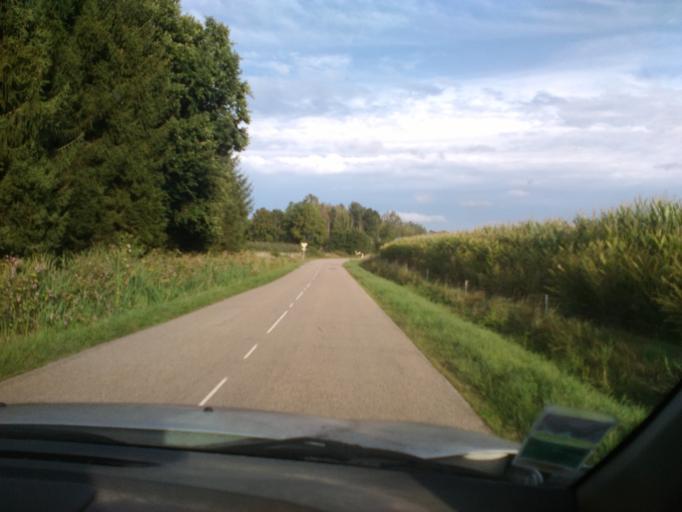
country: FR
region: Lorraine
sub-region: Departement des Vosges
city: Jeanmenil
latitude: 48.3270
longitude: 6.6790
